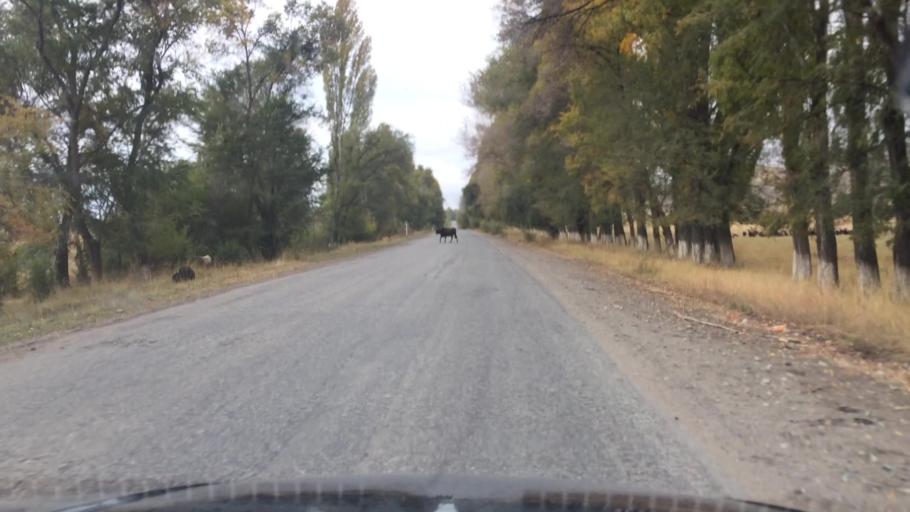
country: KG
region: Ysyk-Koel
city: Pokrovka
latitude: 42.7397
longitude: 77.9003
